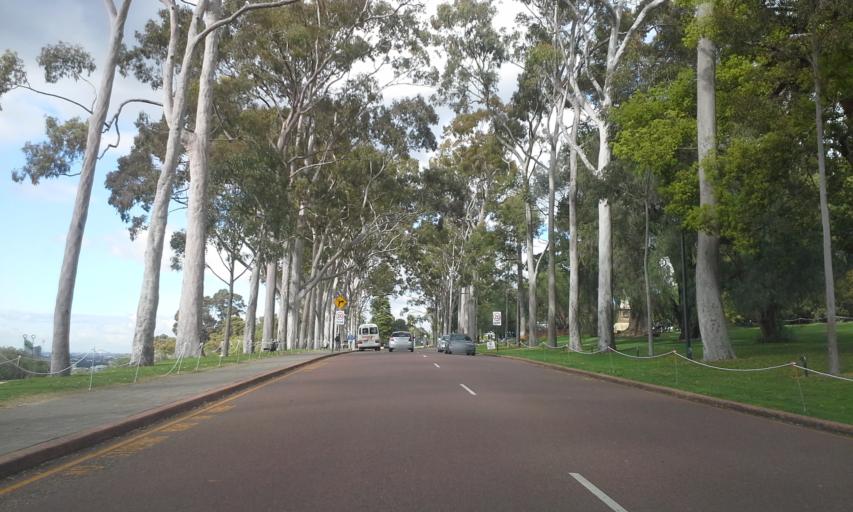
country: AU
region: Western Australia
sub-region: City of Perth
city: West Perth
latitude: -31.9575
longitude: 115.8441
